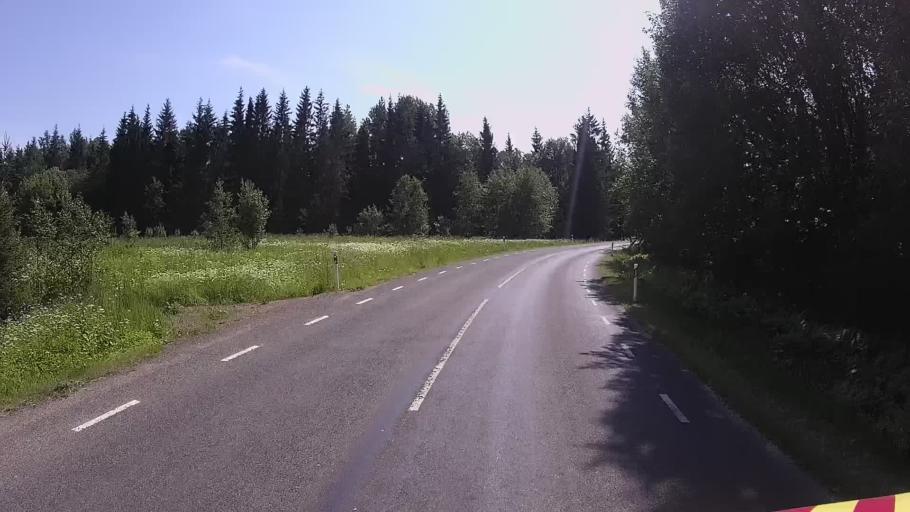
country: EE
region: Viljandimaa
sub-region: Karksi vald
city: Karksi-Nuia
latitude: 58.0386
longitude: 25.5469
